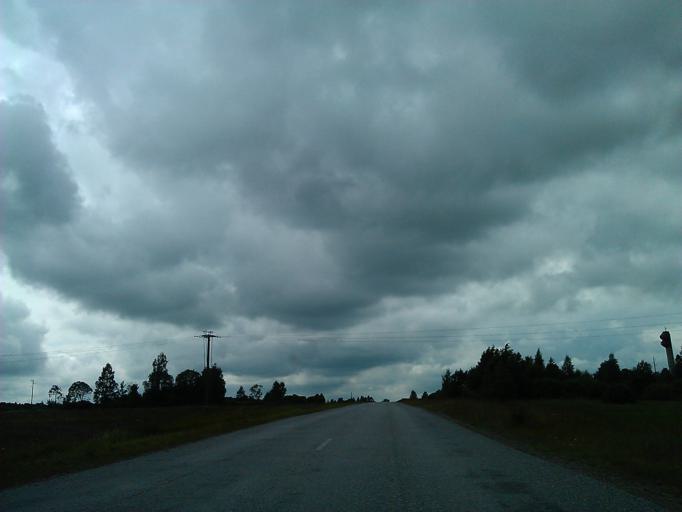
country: LV
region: Aizpute
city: Aizpute
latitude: 56.7993
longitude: 21.6780
